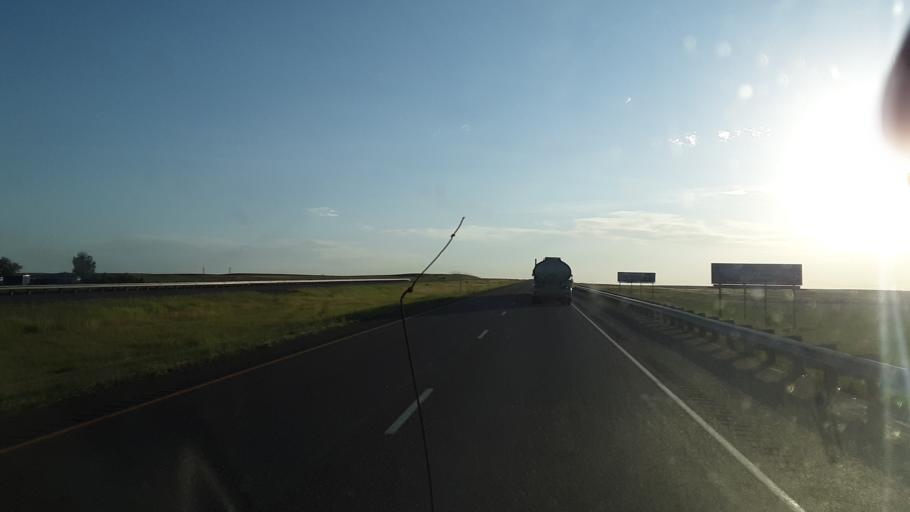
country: US
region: Montana
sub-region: Big Horn County
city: Hardin
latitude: 45.7464
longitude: -107.6375
